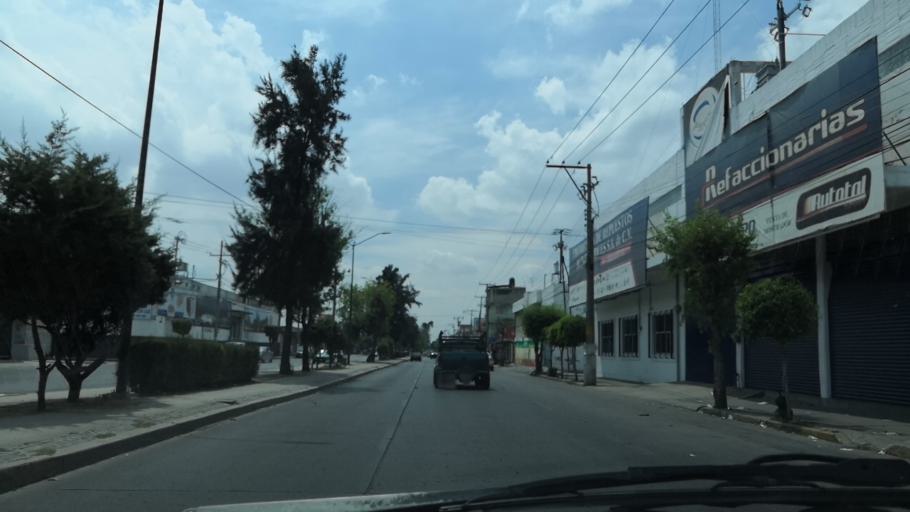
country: MX
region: Guanajuato
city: Leon
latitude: 21.1005
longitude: -101.6795
